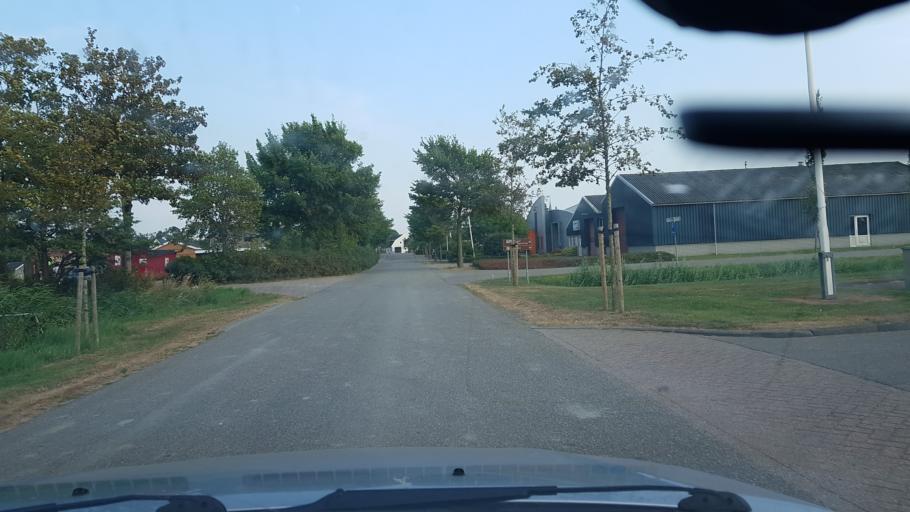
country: NL
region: Friesland
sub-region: Gemeente Ferwerderadiel
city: Burdaard
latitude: 53.2977
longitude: 5.8775
